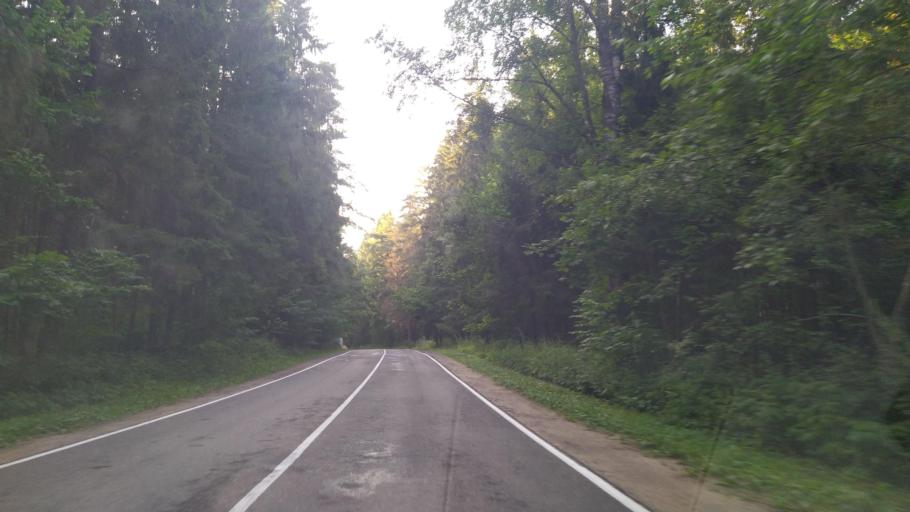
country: RU
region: Pskov
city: Pushkinskiye Gory
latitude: 57.0332
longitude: 28.9199
